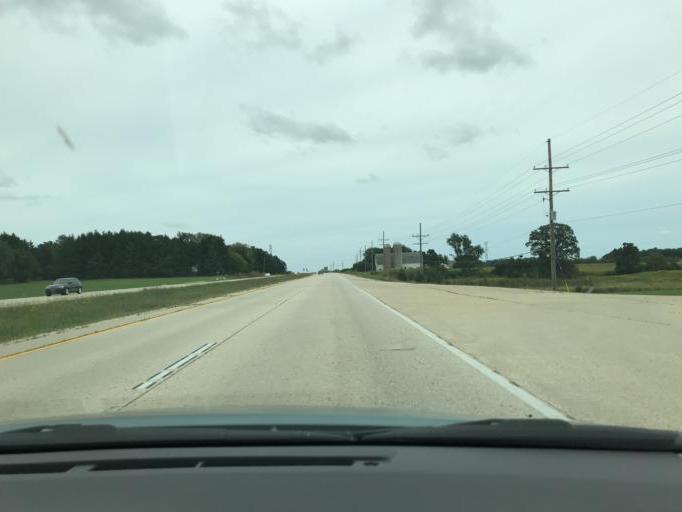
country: US
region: Wisconsin
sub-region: Kenosha County
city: Pleasant Prairie
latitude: 42.5672
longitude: -87.9768
